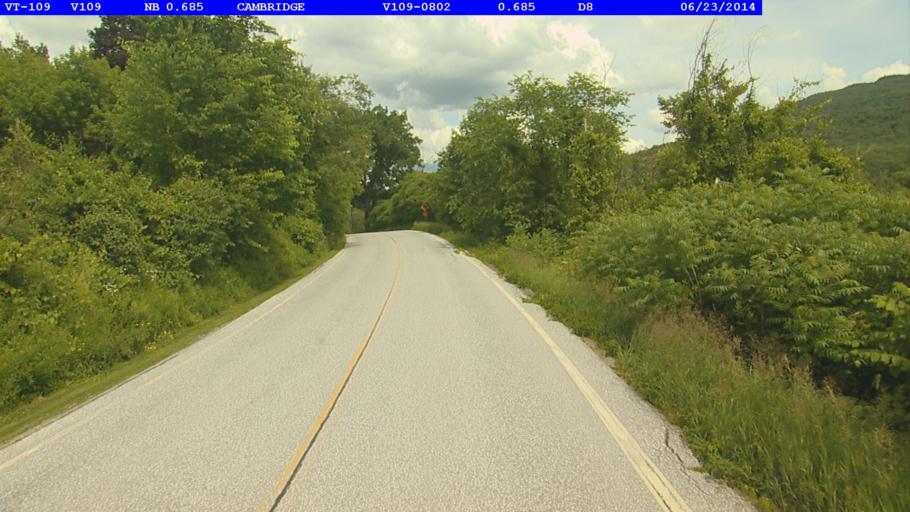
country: US
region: Vermont
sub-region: Lamoille County
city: Johnson
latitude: 44.6528
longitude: -72.8149
